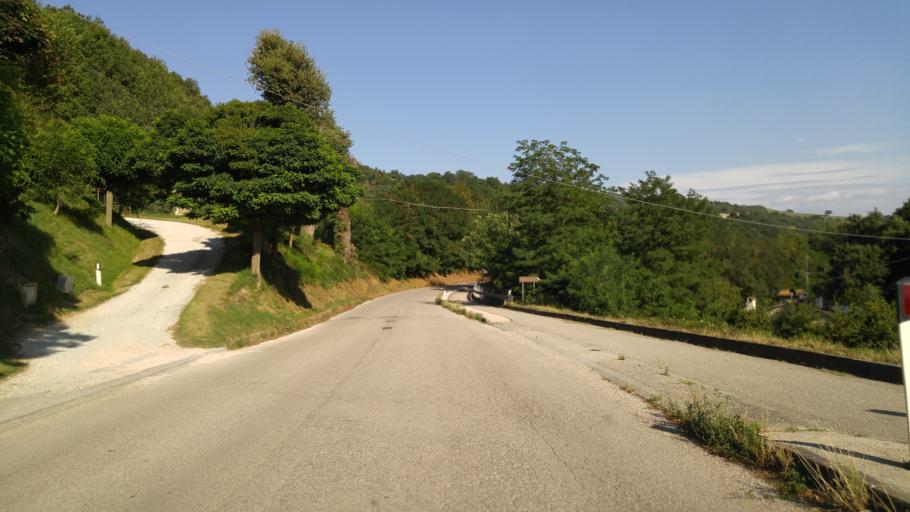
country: IT
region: The Marches
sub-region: Provincia di Pesaro e Urbino
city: Urbania
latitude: 43.6835
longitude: 12.5153
